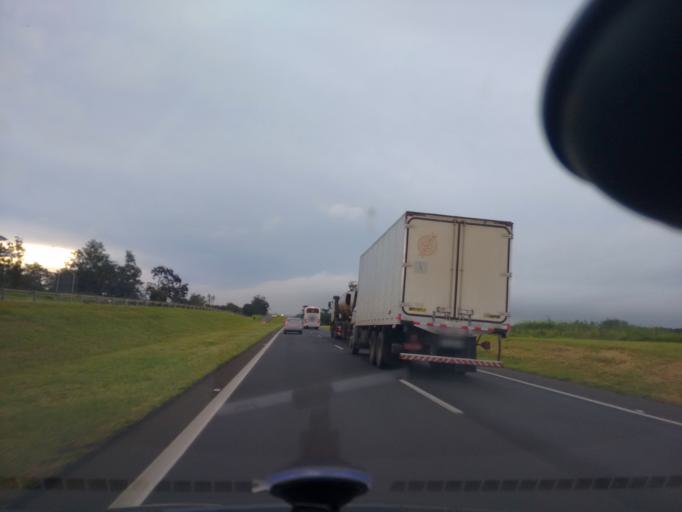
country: BR
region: Sao Paulo
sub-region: Sao Carlos
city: Sao Carlos
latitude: -21.9807
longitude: -47.9184
